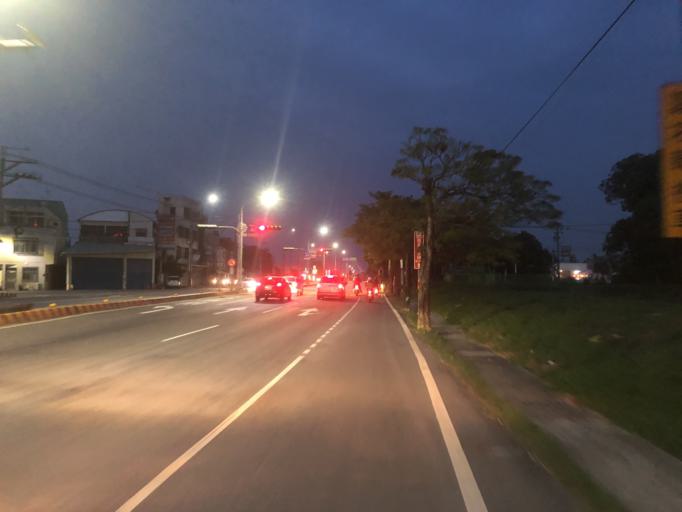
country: TW
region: Taiwan
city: Yujing
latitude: 23.1727
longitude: 120.3383
